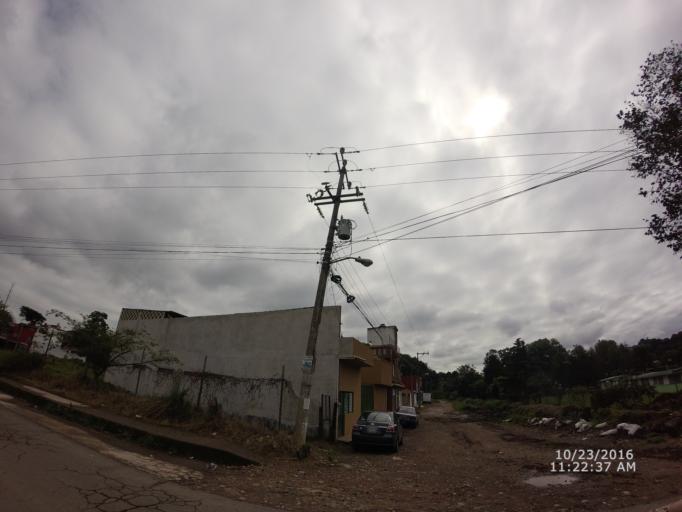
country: MX
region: Veracruz
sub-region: Tlalnelhuayocan
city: Guadalupe Victoria
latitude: 19.5498
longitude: -96.9477
